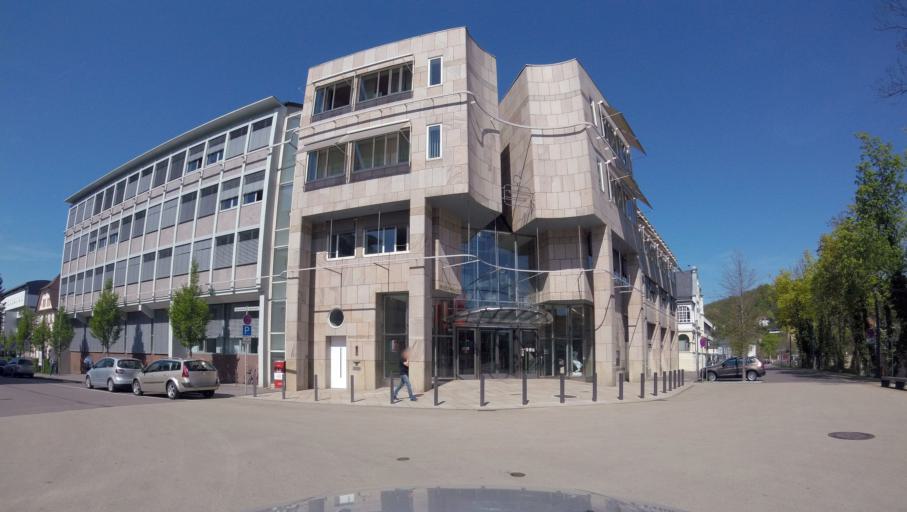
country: DE
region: Baden-Wuerttemberg
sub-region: Regierungsbezirk Stuttgart
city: Schwabisch Gmund
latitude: 48.7981
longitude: 9.7919
